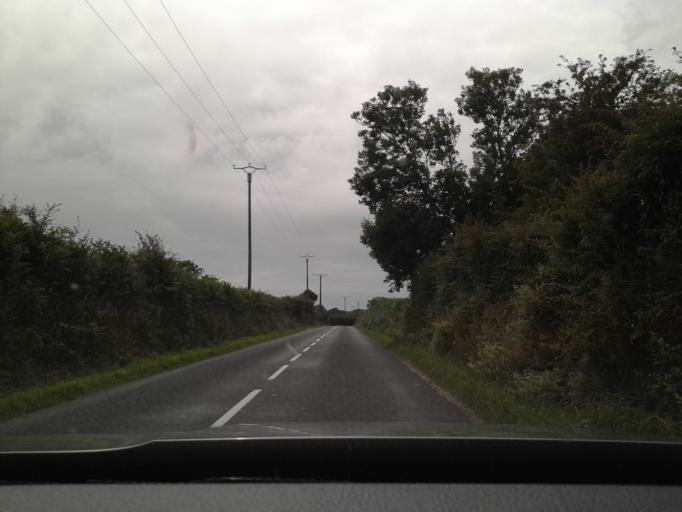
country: FR
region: Lower Normandy
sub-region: Departement de la Manche
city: Urville-Nacqueville
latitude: 49.6747
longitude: -1.7836
